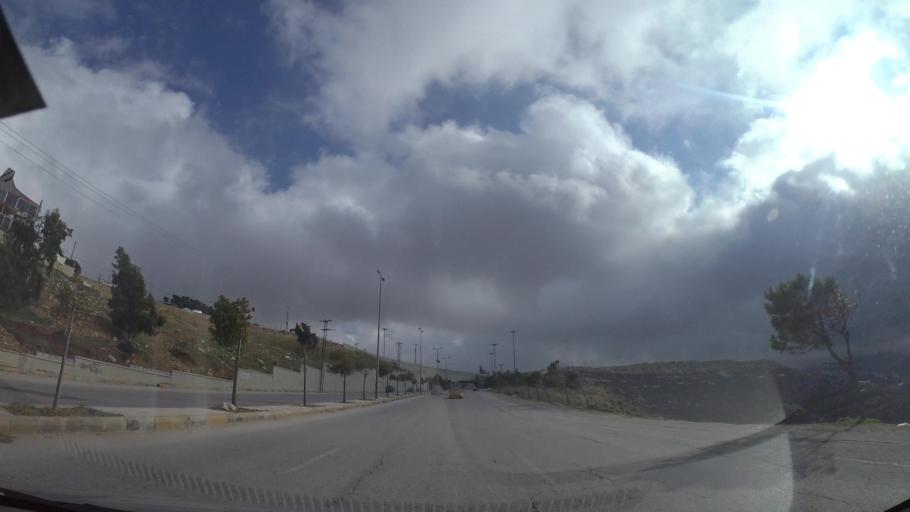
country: JO
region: Amman
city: Al Jubayhah
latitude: 32.0485
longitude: 35.8711
